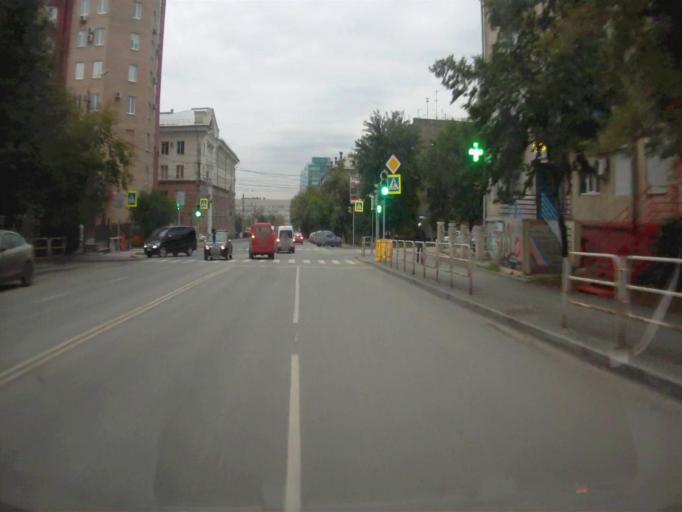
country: RU
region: Chelyabinsk
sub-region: Gorod Chelyabinsk
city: Chelyabinsk
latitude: 55.1549
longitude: 61.3988
